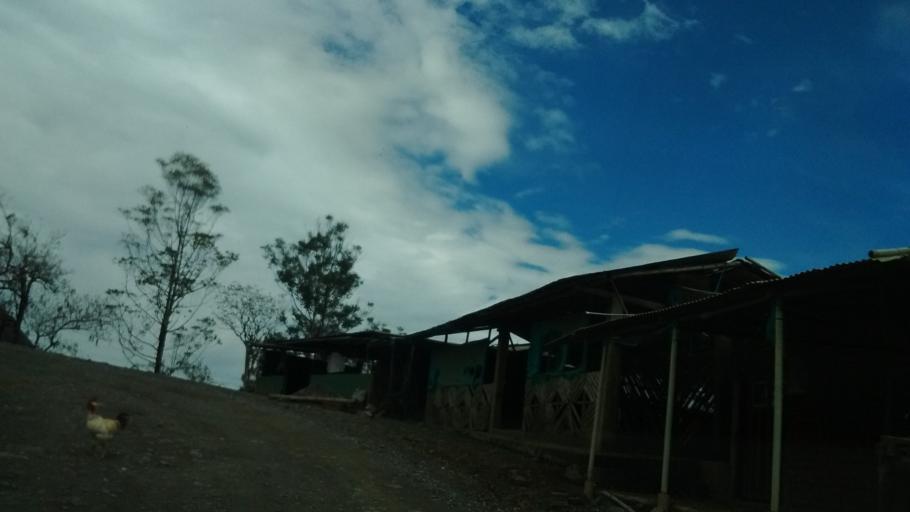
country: CO
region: Cauca
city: Almaguer
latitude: 1.8631
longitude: -76.9325
